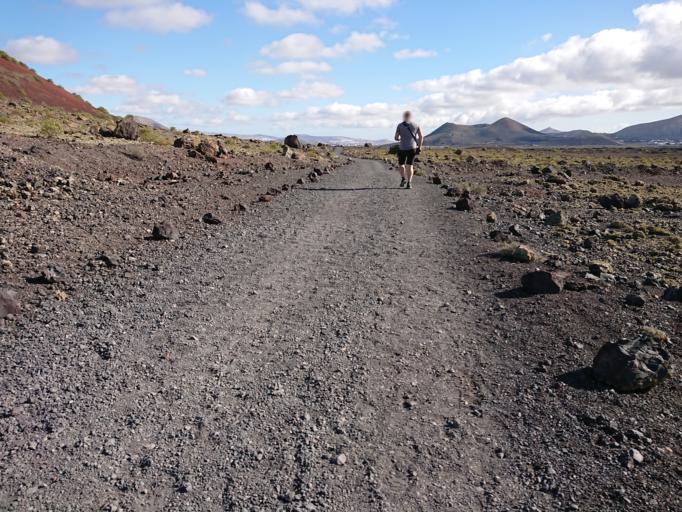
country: ES
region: Canary Islands
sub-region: Provincia de Las Palmas
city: Tias
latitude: 29.0030
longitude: -13.6788
